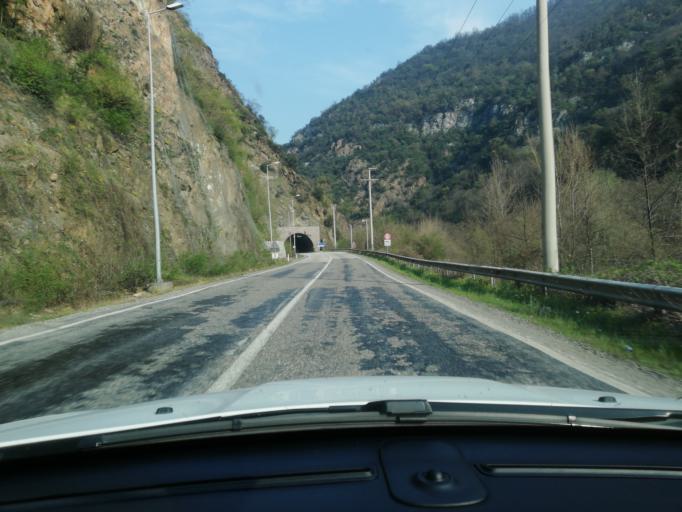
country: TR
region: Karabuk
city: Yenice
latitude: 41.1598
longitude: 32.4595
